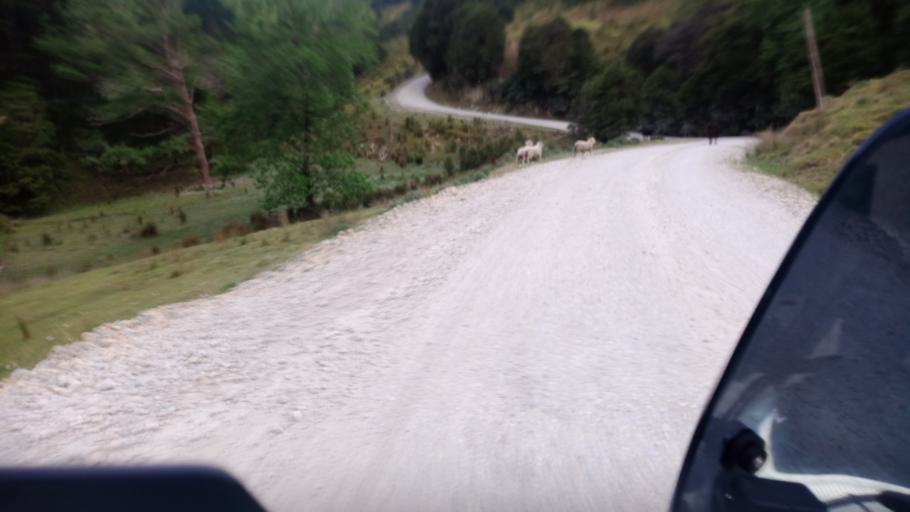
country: NZ
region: Gisborne
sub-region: Gisborne District
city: Gisborne
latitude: -38.4806
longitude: 177.9647
